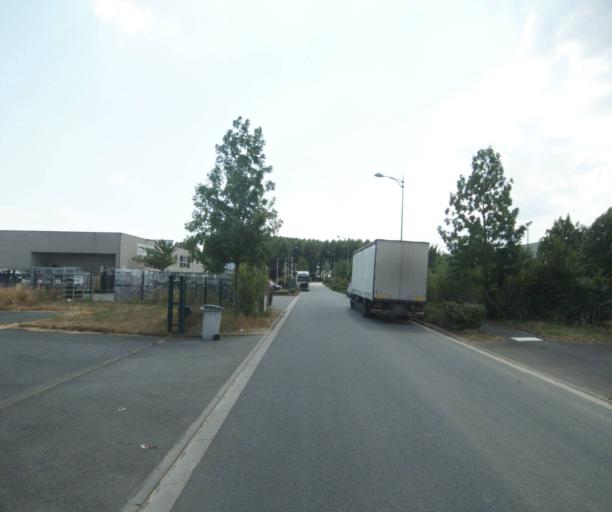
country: FR
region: Nord-Pas-de-Calais
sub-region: Departement du Nord
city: Comines
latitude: 50.7527
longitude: 2.9947
